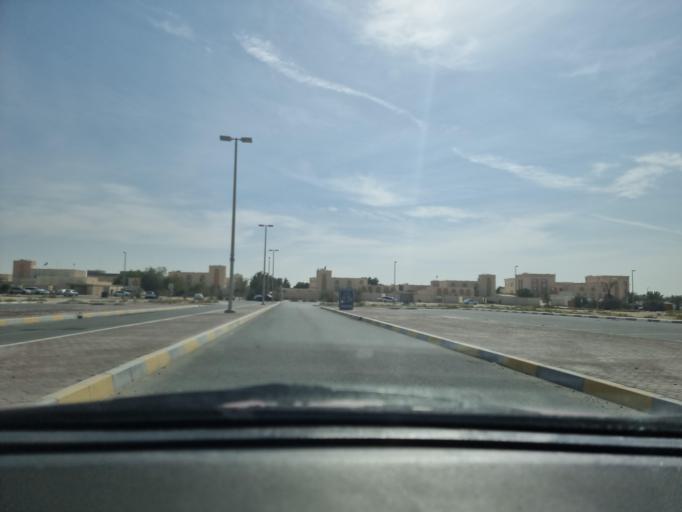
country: AE
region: Abu Dhabi
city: Abu Dhabi
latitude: 24.3852
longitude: 54.6977
